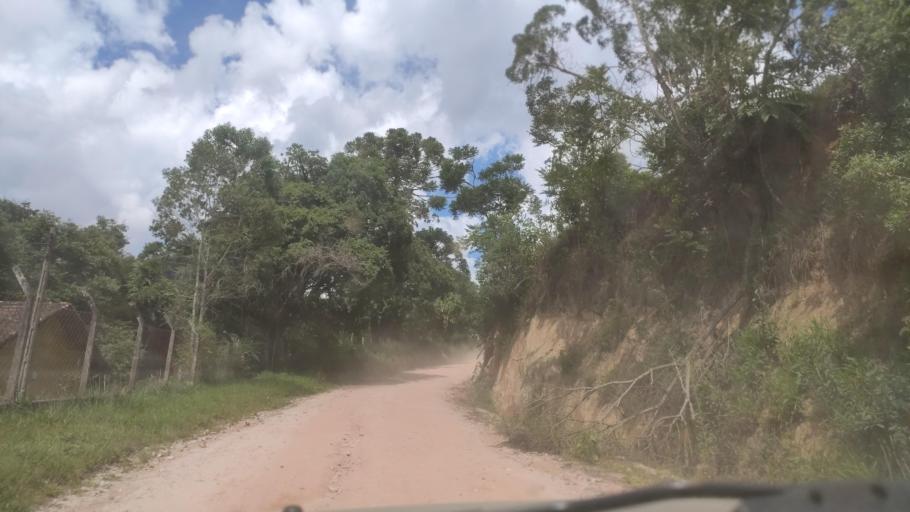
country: BR
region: Minas Gerais
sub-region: Camanducaia
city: Camanducaia
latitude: -22.7681
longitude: -45.9899
